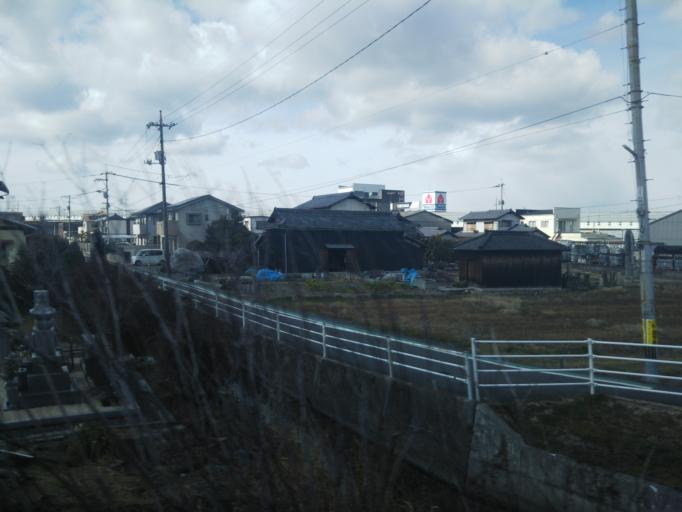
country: JP
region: Okayama
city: Okayama-shi
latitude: 34.6222
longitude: 133.8903
